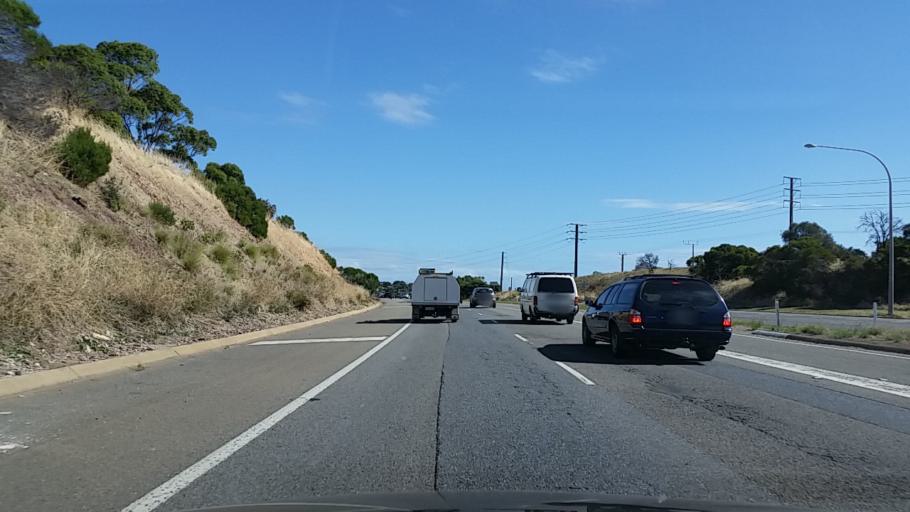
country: AU
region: South Australia
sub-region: Onkaparinga
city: Morphett Vale
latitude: -35.1135
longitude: 138.4918
